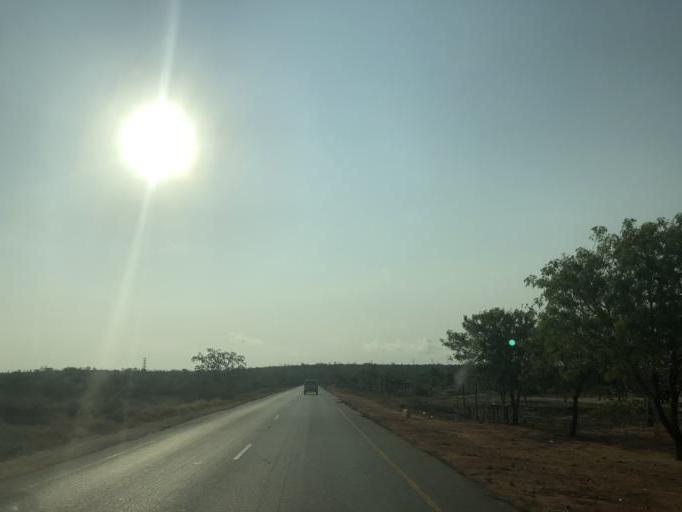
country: AO
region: Luanda
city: Luanda
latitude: -9.1836
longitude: 13.0635
